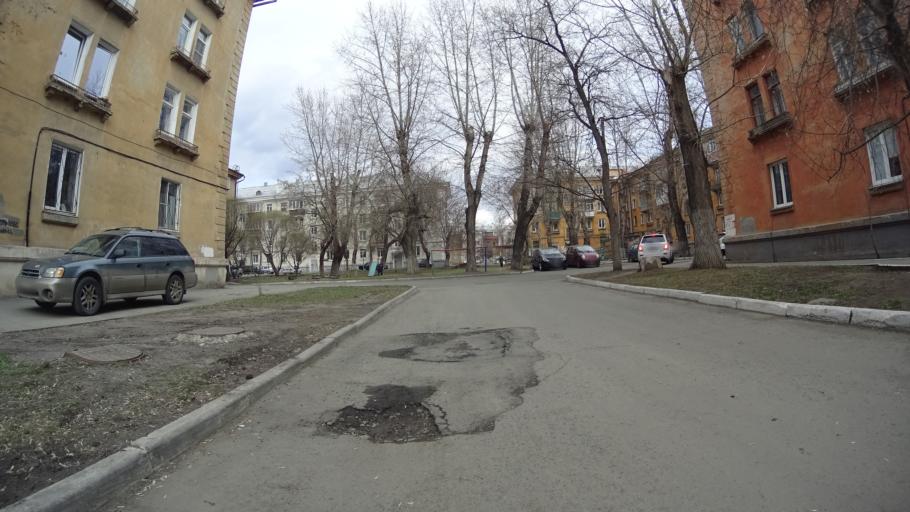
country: RU
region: Chelyabinsk
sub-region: Gorod Chelyabinsk
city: Chelyabinsk
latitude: 55.1629
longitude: 61.4394
